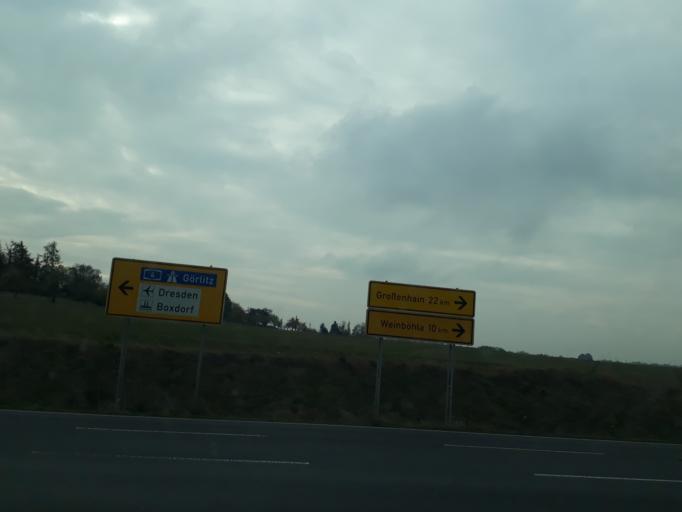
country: DE
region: Saxony
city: Moritzburg
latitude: 51.1372
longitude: 13.6819
